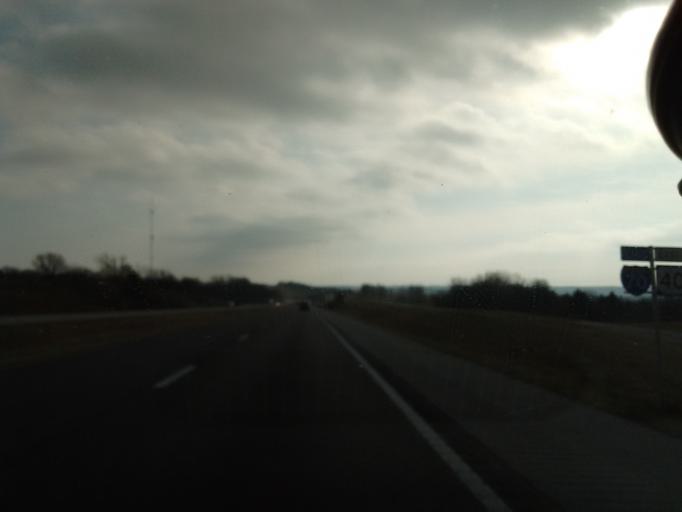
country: US
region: Missouri
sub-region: Cooper County
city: Boonville
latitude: 38.9405
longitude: -92.9858
